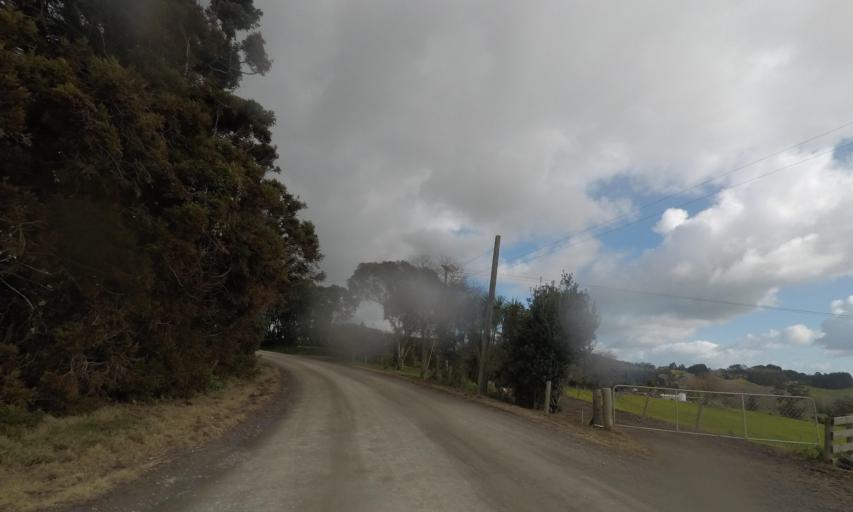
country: NZ
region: Auckland
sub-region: Auckland
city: Wellsford
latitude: -36.1620
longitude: 174.6038
